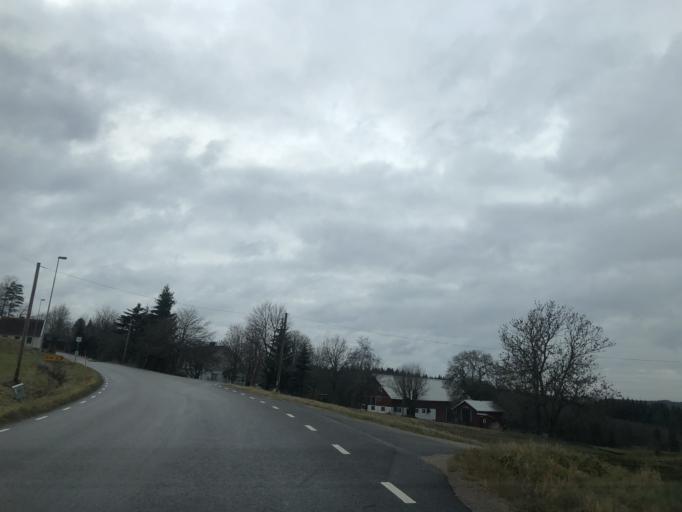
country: SE
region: Vaestra Goetaland
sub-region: Ulricehamns Kommun
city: Ulricehamn
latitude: 57.8280
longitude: 13.2498
